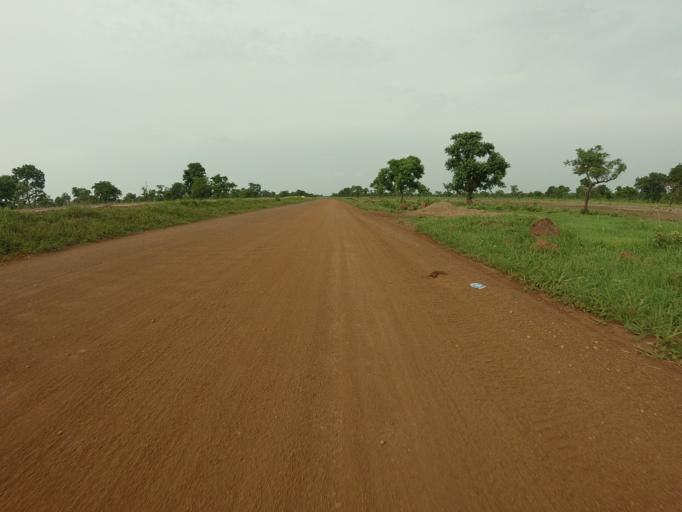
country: GH
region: Northern
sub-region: Yendi
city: Yendi
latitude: 9.7873
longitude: -0.1161
